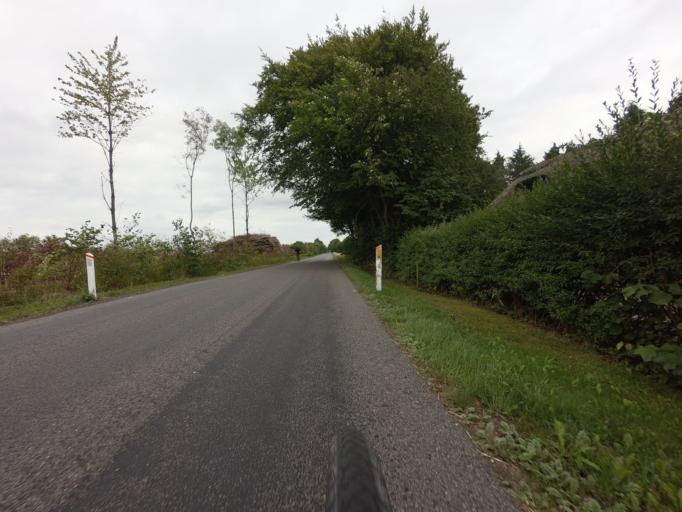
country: DK
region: Zealand
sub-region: Stevns Kommune
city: Store Heddinge
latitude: 55.3151
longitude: 12.3483
